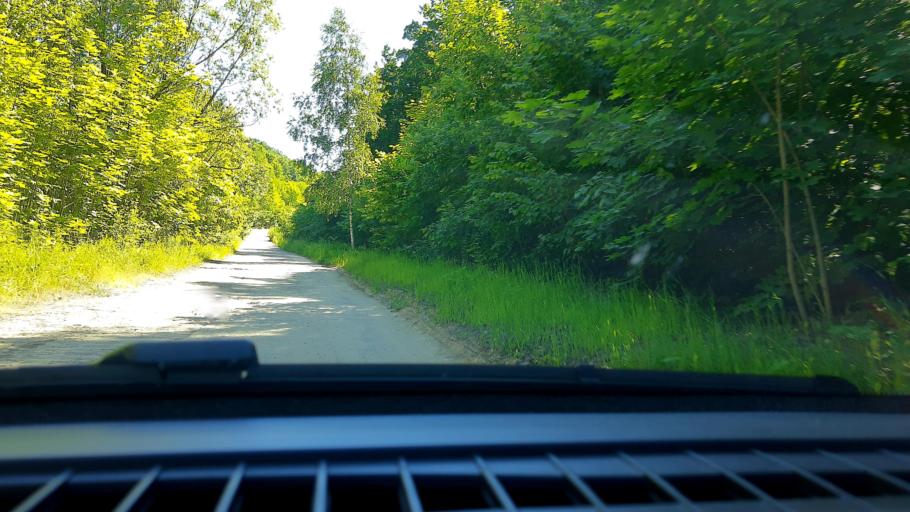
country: RU
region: Nizjnij Novgorod
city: Nizhniy Novgorod
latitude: 56.2247
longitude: 43.9190
